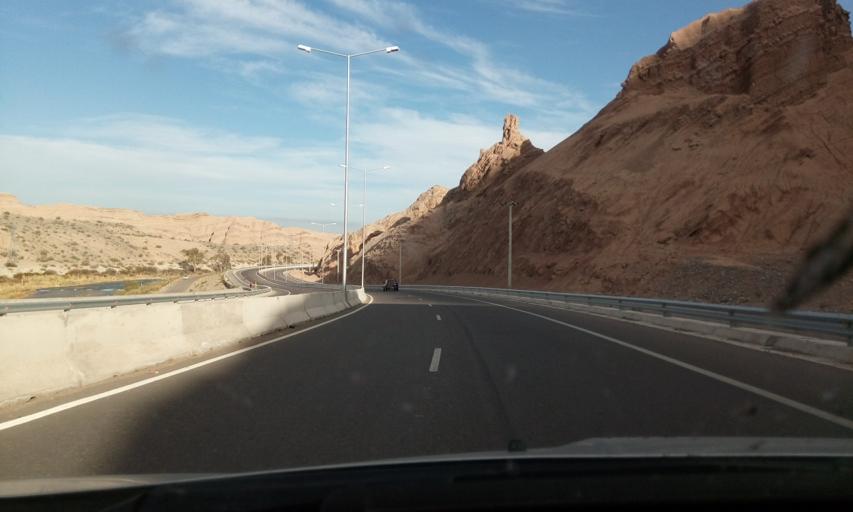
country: AR
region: San Juan
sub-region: Departamento de Rivadavia
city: Rivadavia
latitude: -31.4813
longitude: -68.6504
